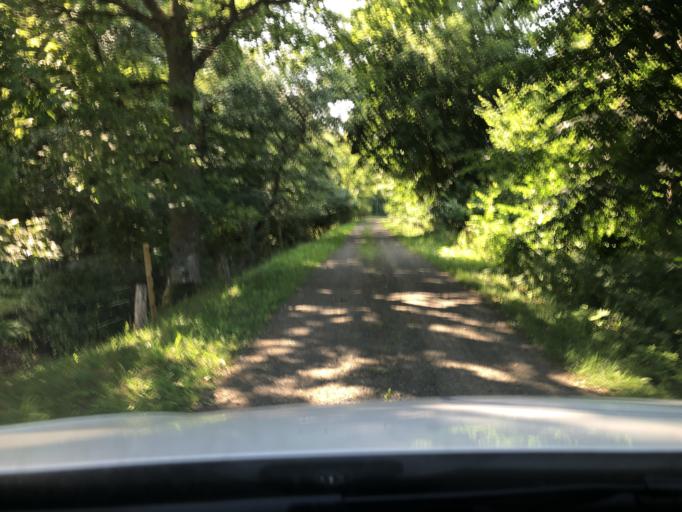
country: SE
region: Skane
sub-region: Kristianstads Kommun
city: Degeberga
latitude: 55.8023
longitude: 14.1418
